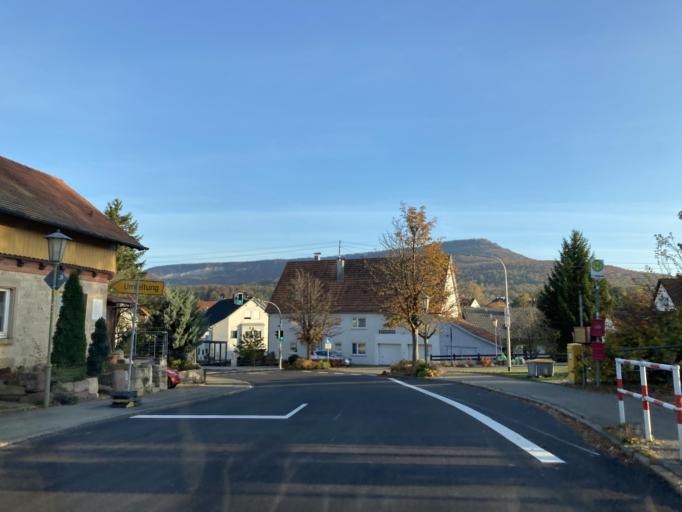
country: DE
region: Baden-Wuerttemberg
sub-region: Tuebingen Region
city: Ofterdingen
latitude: 48.3957
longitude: 9.0304
